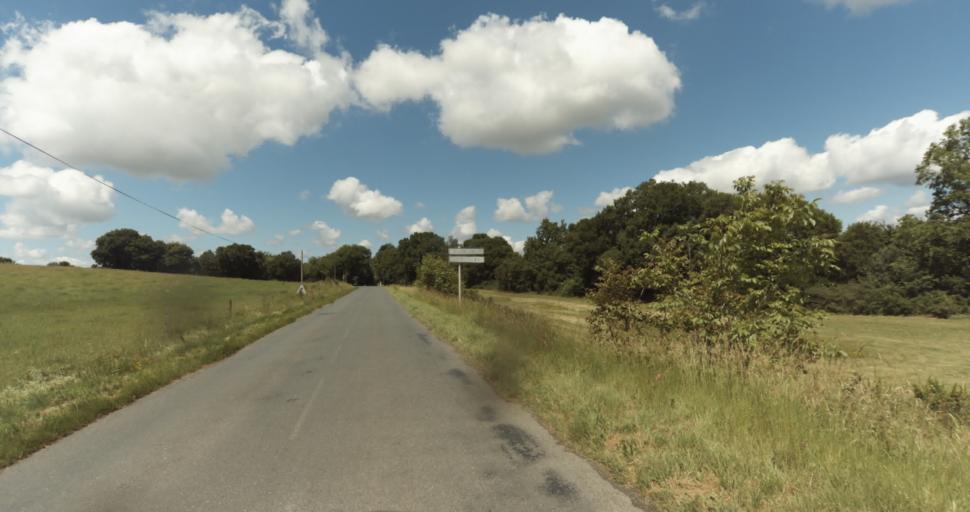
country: FR
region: Aquitaine
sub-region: Departement de la Dordogne
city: Beaumont-du-Perigord
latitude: 44.7529
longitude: 0.6985
